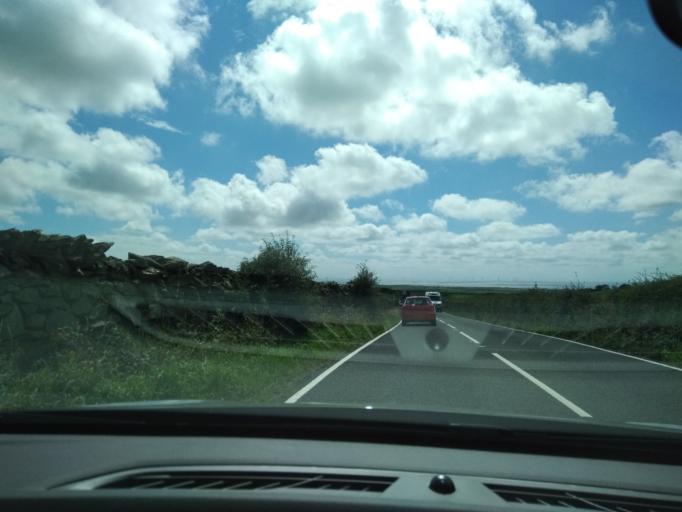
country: GB
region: England
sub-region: Cumbria
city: Millom
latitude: 54.2386
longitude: -3.3213
